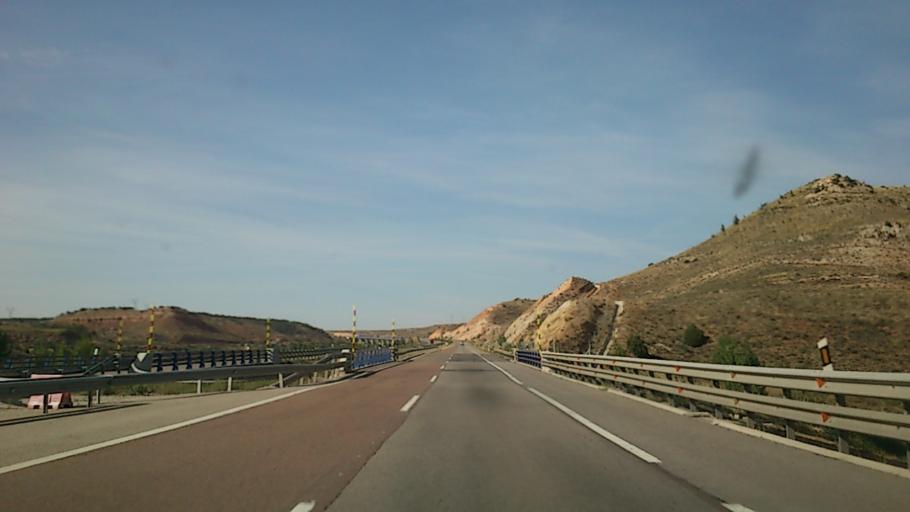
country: ES
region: Aragon
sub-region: Provincia de Teruel
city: Calamocha
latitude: 40.9790
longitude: -1.2596
